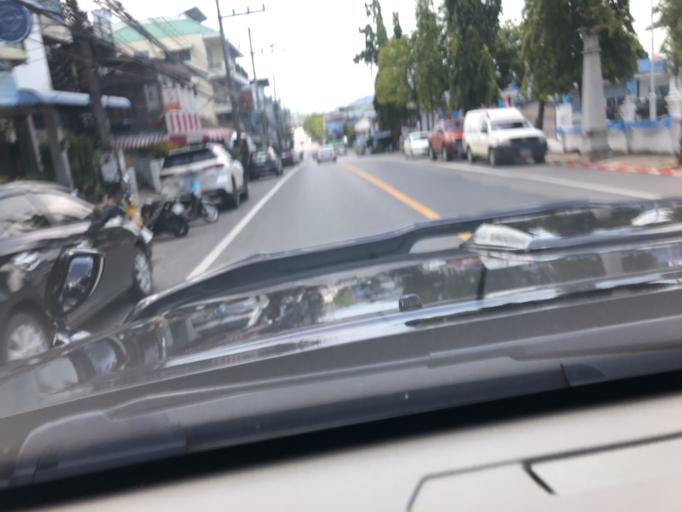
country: TH
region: Krabi
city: Krabi
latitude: 8.0612
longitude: 98.9184
